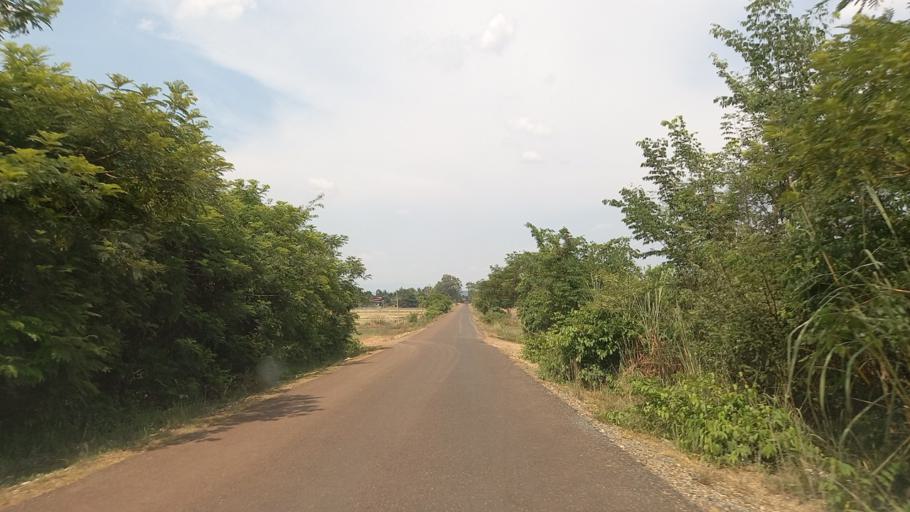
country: LA
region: Bolikhamxai
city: Muang Pakxan
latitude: 18.4290
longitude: 103.7337
